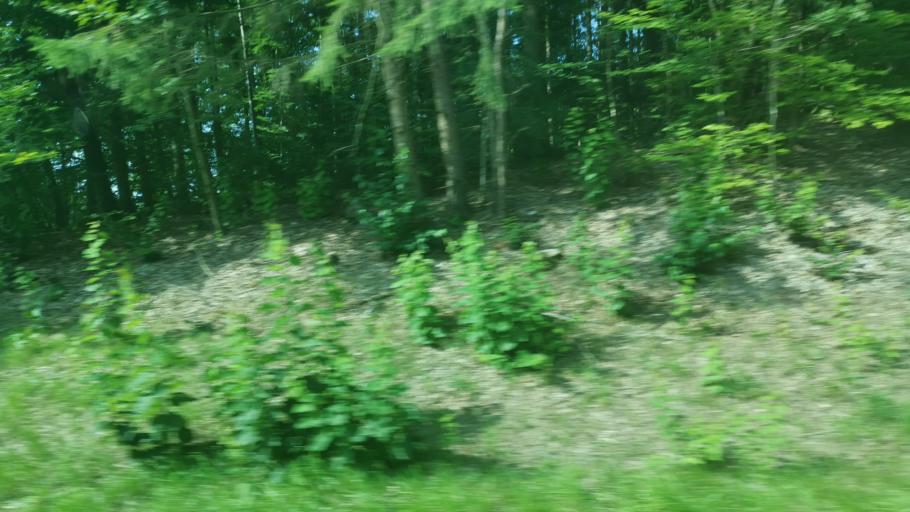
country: DE
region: Bavaria
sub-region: Upper Palatinate
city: Pemfling
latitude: 49.2737
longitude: 12.6302
